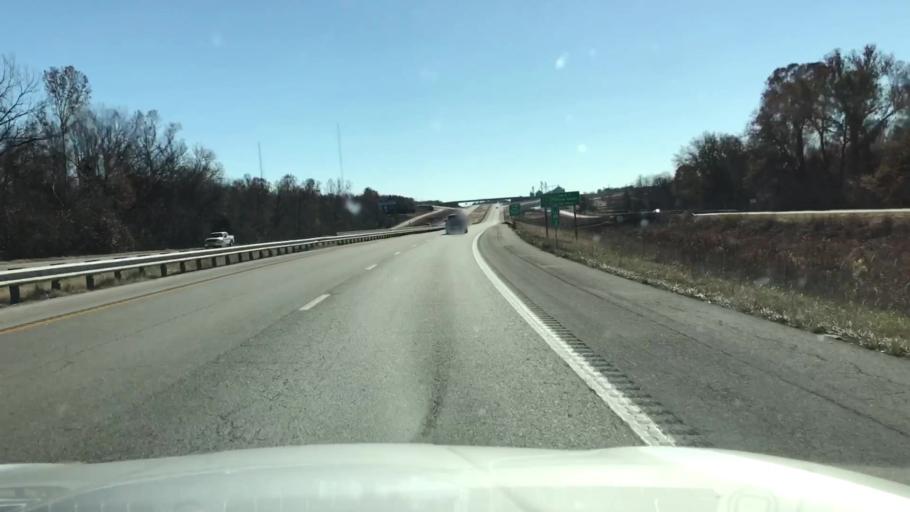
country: US
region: Missouri
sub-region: Jasper County
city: Carthage
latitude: 37.1076
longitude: -94.3101
